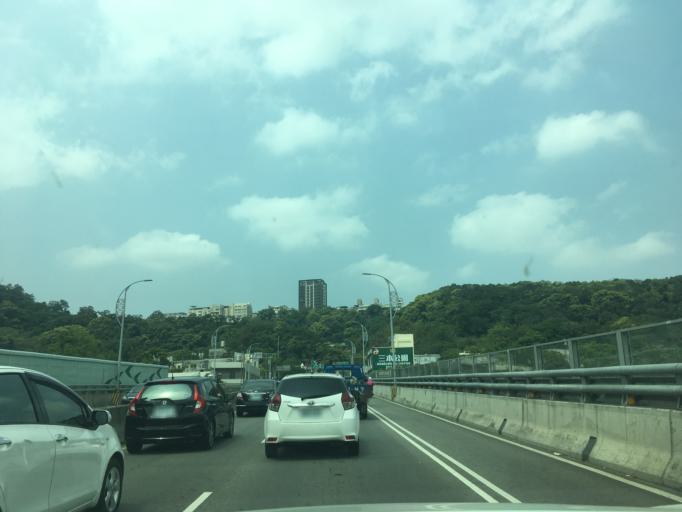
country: TW
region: Taiwan
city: Daxi
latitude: 24.8909
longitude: 121.2805
